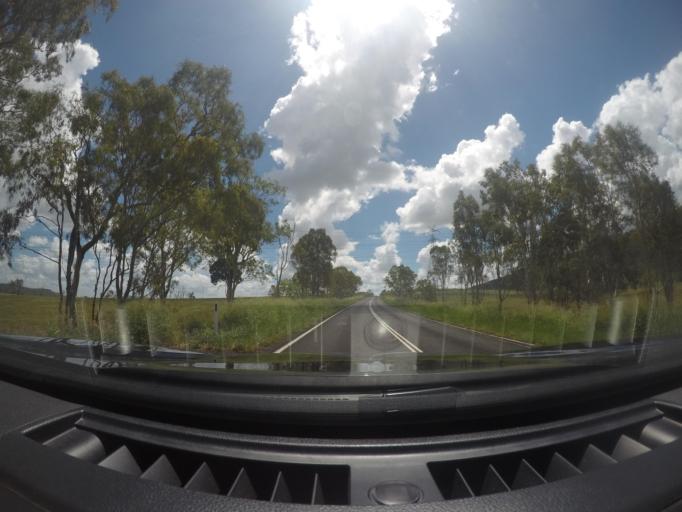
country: AU
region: Queensland
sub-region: Moreton Bay
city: D'Aguilar
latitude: -27.1508
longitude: 152.5443
